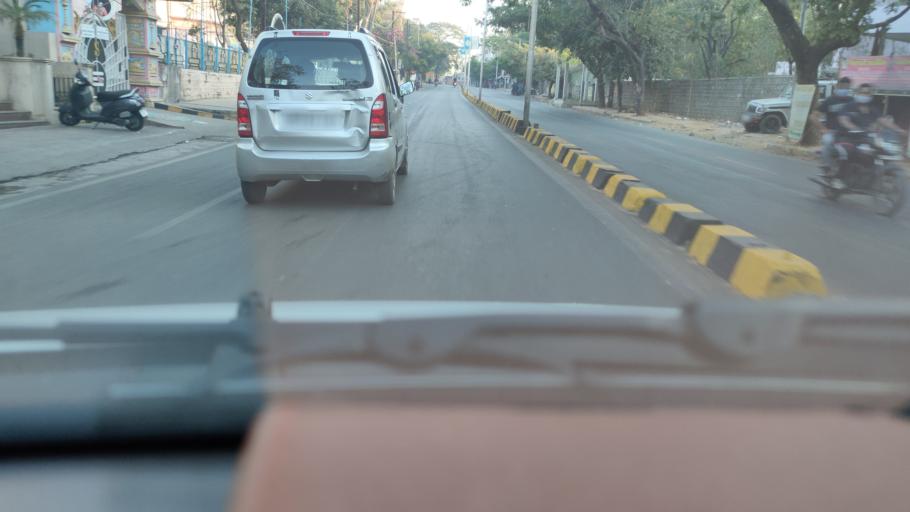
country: IN
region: Telangana
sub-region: Rangareddi
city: Gaddi Annaram
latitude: 17.4021
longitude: 78.5141
